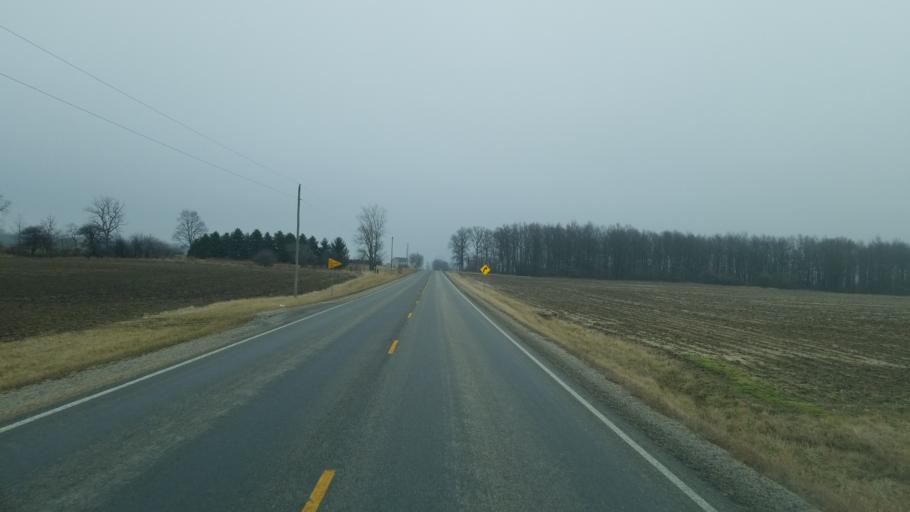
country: US
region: Indiana
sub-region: Adams County
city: Geneva
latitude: 40.5474
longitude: -85.0102
